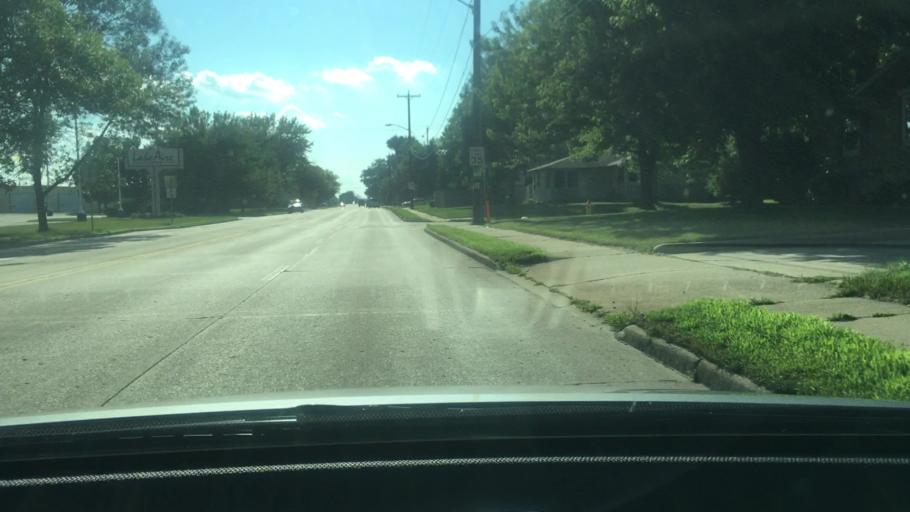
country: US
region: Wisconsin
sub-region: Winnebago County
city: Oshkosh
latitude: 43.9959
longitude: -88.5433
